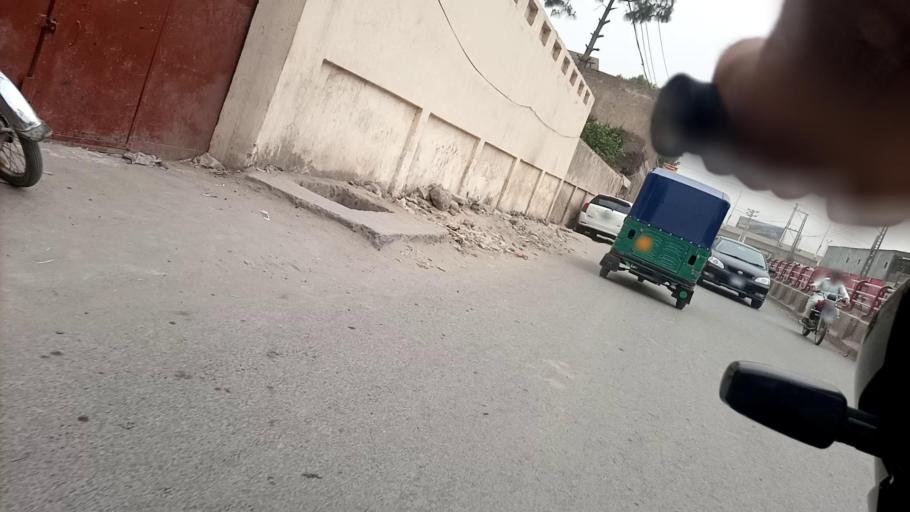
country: PK
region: Khyber Pakhtunkhwa
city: Peshawar
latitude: 34.0173
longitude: 71.5928
